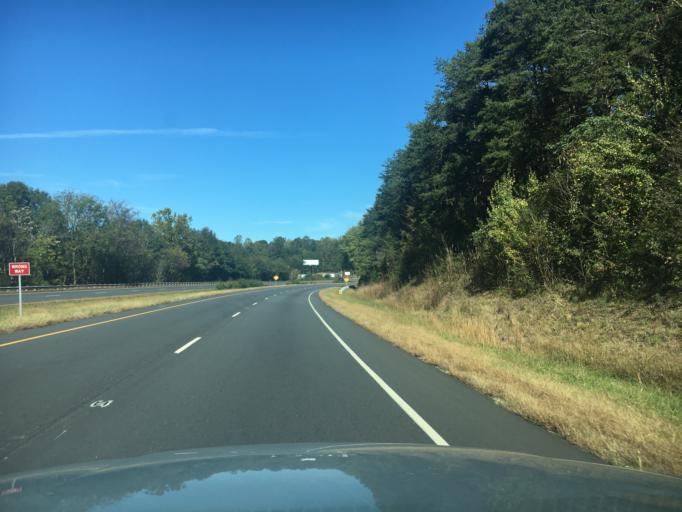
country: US
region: North Carolina
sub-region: Rutherford County
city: Spindale
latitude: 35.3530
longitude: -81.9425
